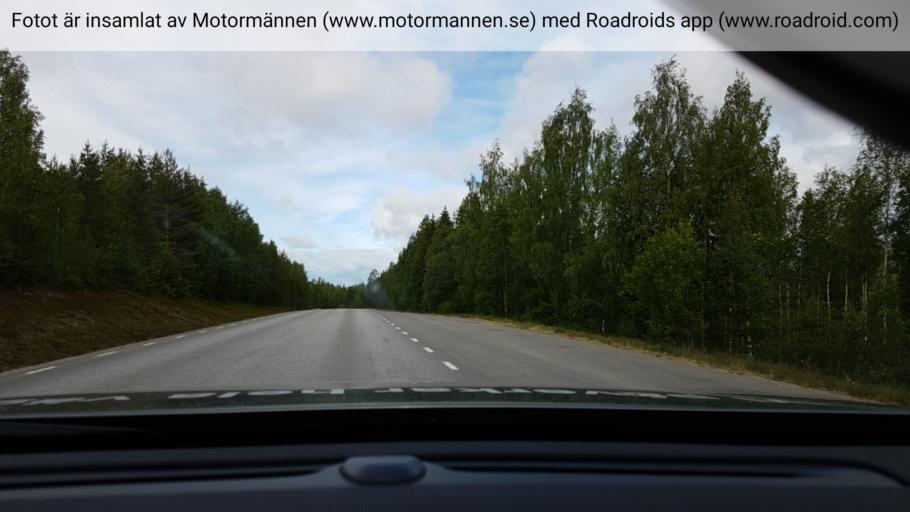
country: SE
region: Vaesterbotten
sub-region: Lycksele Kommun
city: Lycksele
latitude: 64.0611
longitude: 18.4970
